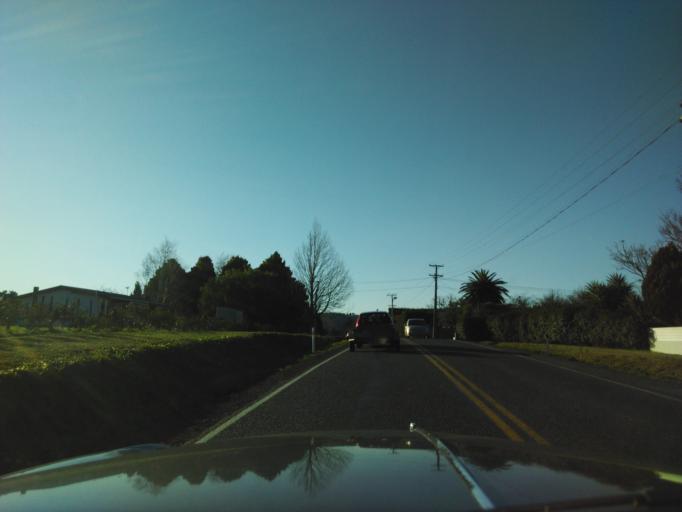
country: NZ
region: Auckland
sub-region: Auckland
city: Rosebank
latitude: -36.7691
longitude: 174.5871
